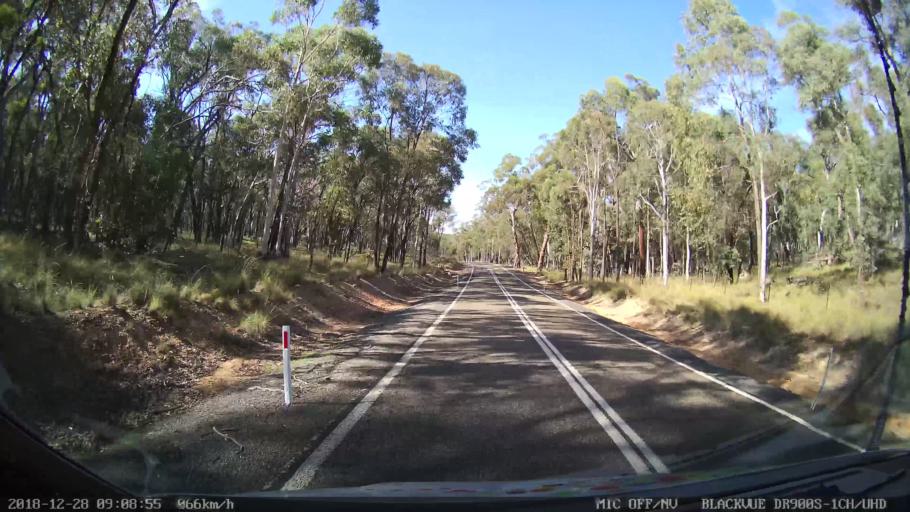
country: AU
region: New South Wales
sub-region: Upper Lachlan Shire
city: Crookwell
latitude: -34.2163
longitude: 149.3365
